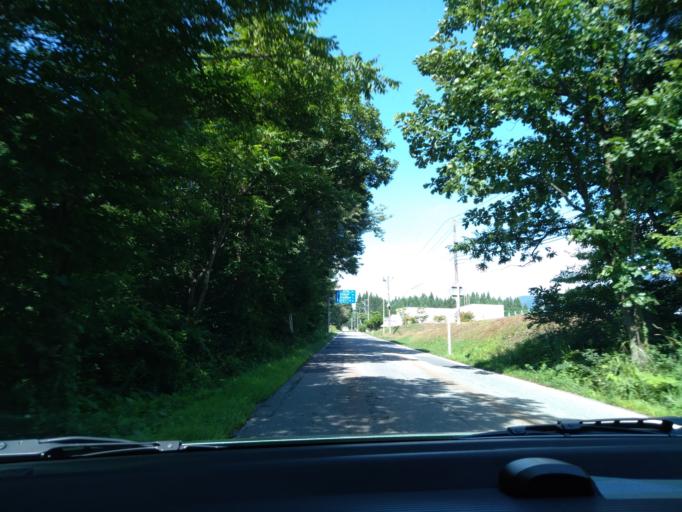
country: JP
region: Akita
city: Kakunodatemachi
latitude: 39.7476
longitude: 140.7216
